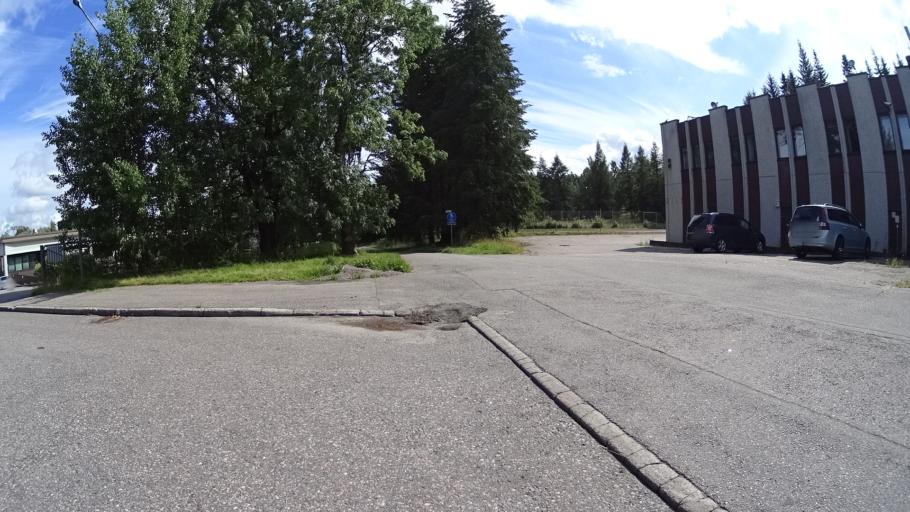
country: FI
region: Uusimaa
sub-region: Helsinki
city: Kilo
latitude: 60.2076
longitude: 24.7590
